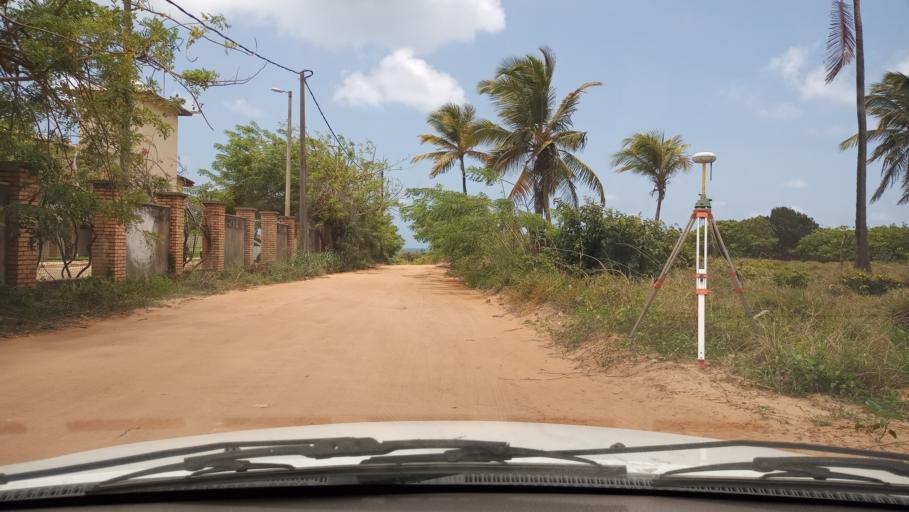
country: BR
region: Rio Grande do Norte
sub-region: Ares
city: Ares
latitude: -6.2370
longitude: -35.0393
